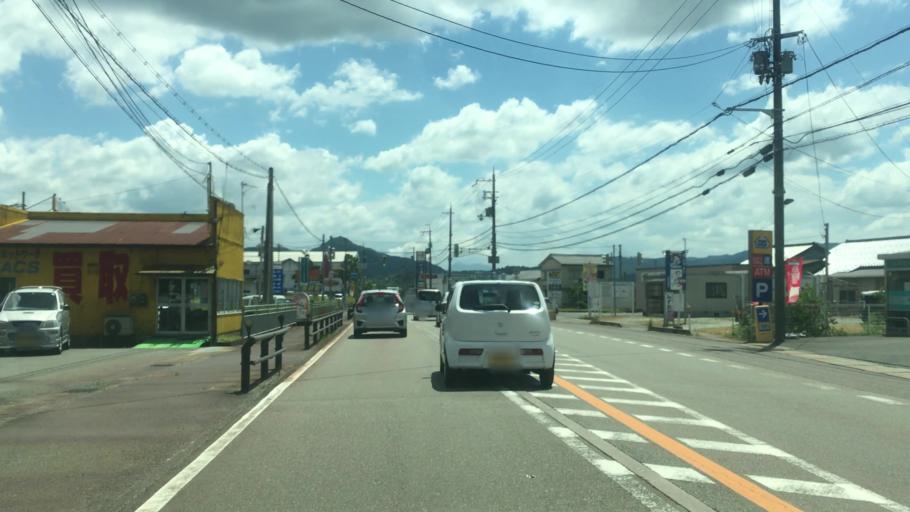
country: JP
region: Hyogo
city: Toyooka
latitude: 35.4937
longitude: 134.8010
